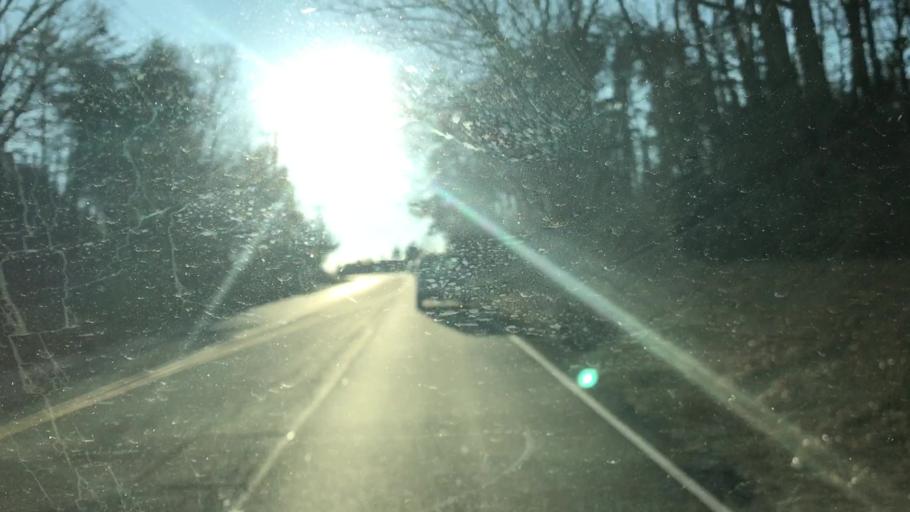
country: US
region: Virginia
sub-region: City of Fredericksburg
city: Fredericksburg
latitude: 38.2862
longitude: -77.4776
